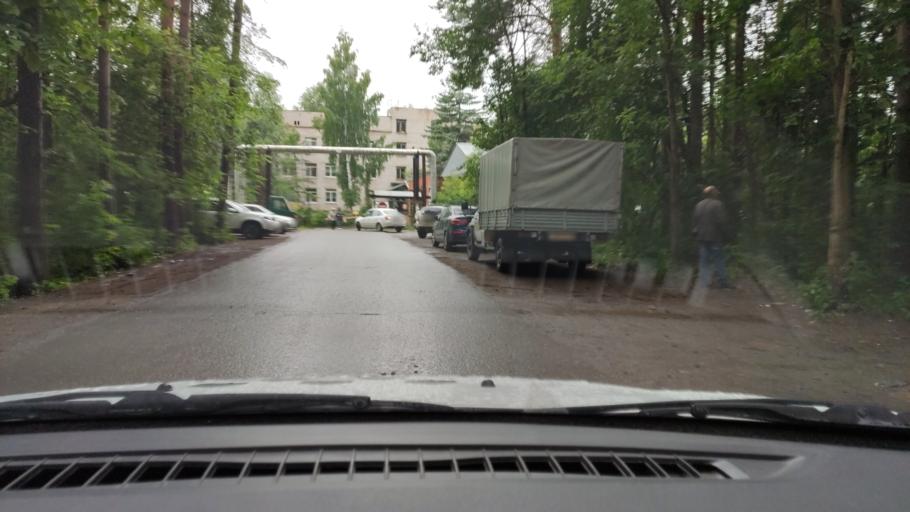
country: RU
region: Udmurtiya
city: Izhevsk
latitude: 56.8850
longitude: 53.1844
